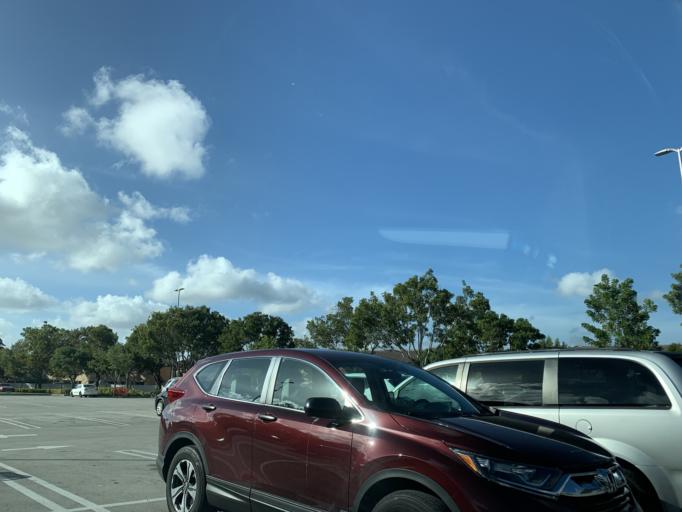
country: US
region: Florida
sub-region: Miami-Dade County
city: The Hammocks
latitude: 25.6851
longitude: -80.4385
